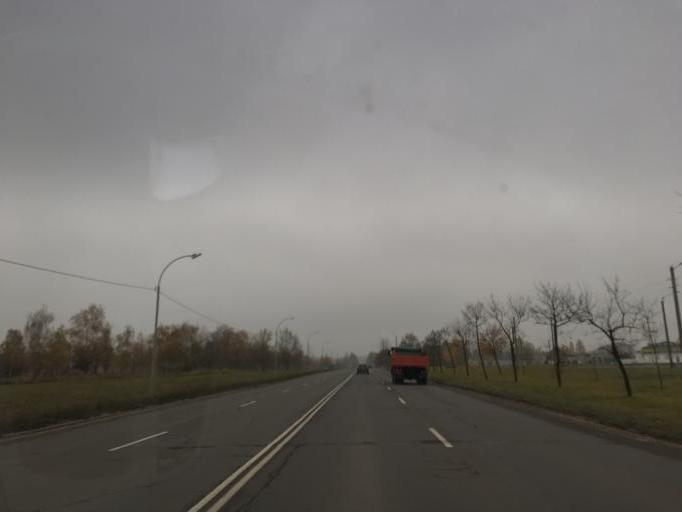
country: BY
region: Mogilev
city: Buynichy
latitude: 53.8614
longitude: 30.3230
